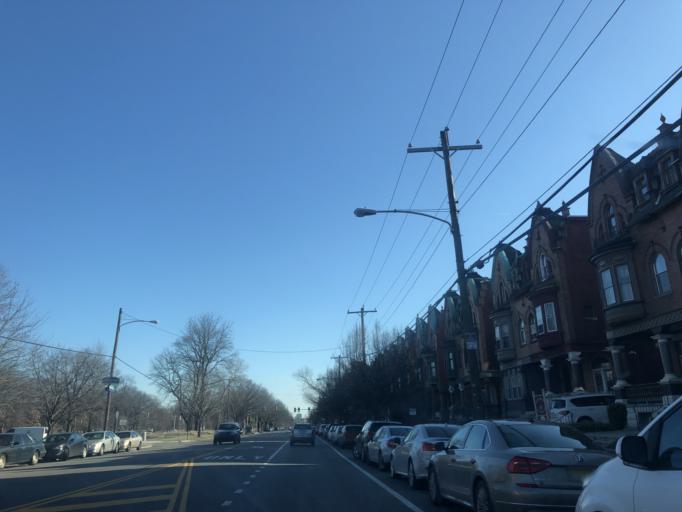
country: US
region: Pennsylvania
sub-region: Montgomery County
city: Bala-Cynwyd
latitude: 39.9769
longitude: -75.2112
